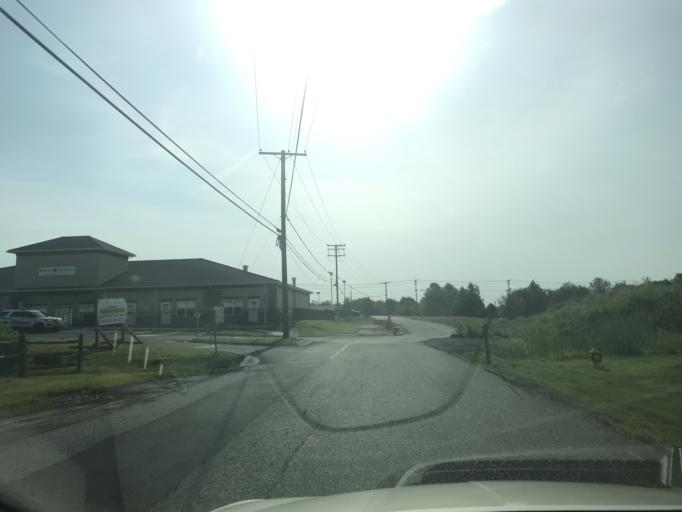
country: US
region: Maryland
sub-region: Harford County
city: Bel Air North
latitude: 39.5667
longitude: -76.3563
